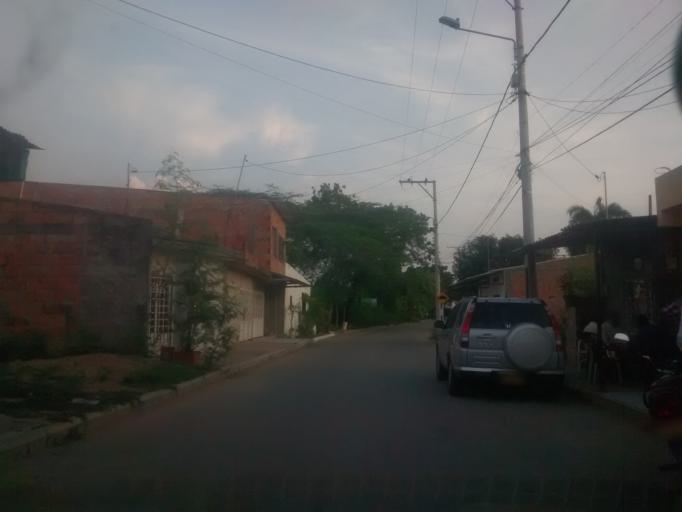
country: CO
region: Cundinamarca
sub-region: Girardot
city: Girardot City
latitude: 4.3199
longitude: -74.7846
